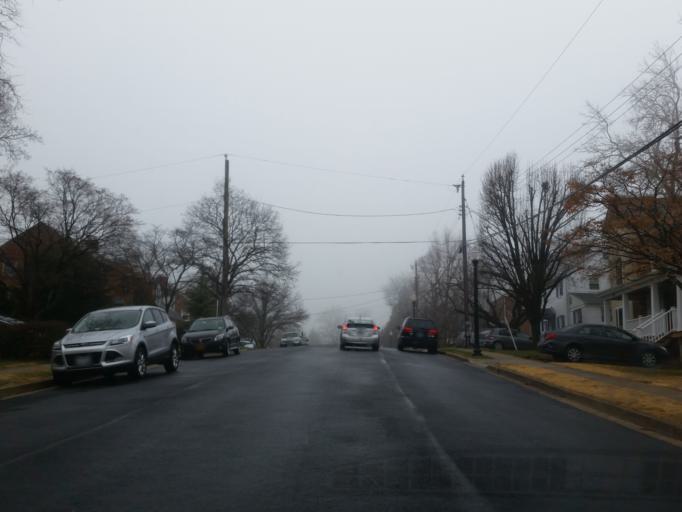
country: US
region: Virginia
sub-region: Fairfax County
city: Seven Corners
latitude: 38.8798
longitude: -77.1497
